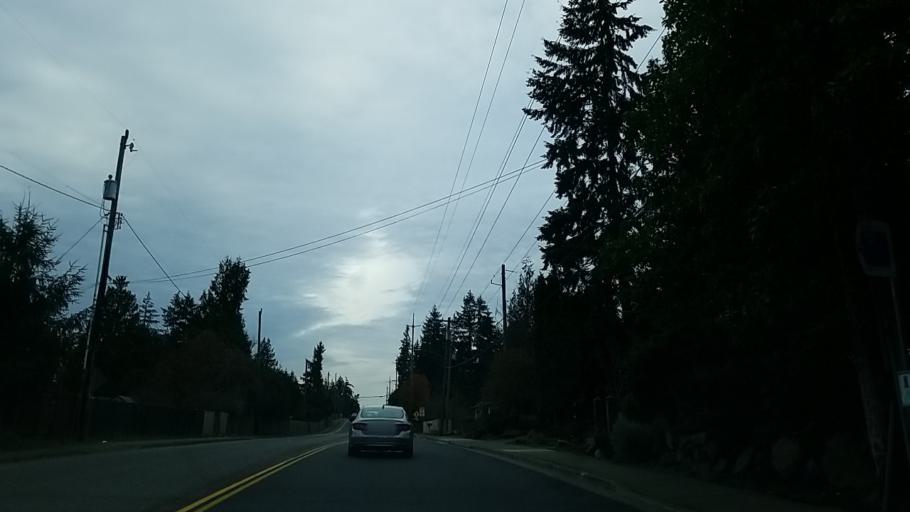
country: US
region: Washington
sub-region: Snohomish County
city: Esperance
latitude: 47.7778
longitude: -122.3485
